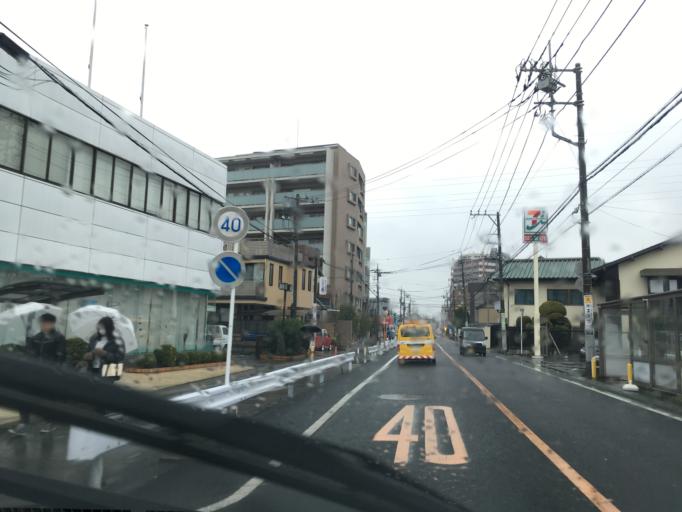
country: JP
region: Saitama
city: Koshigaya
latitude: 35.8852
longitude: 139.7837
